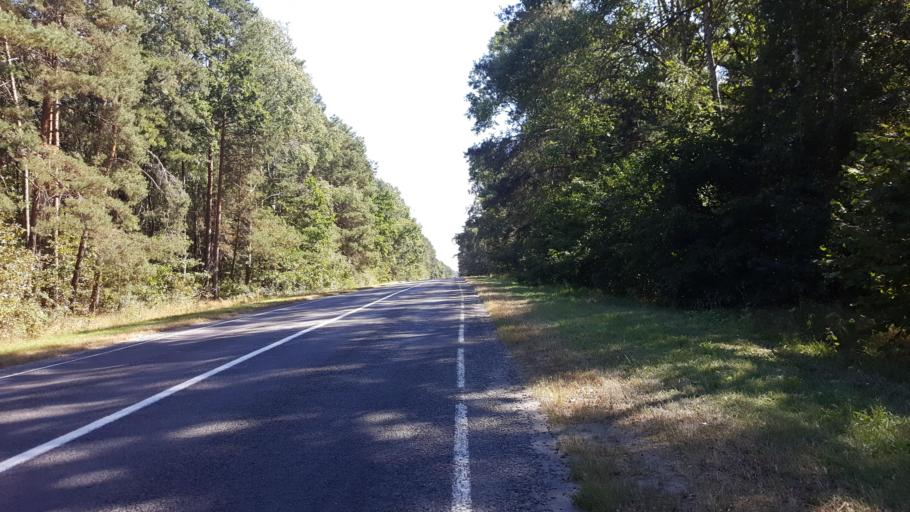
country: PL
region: Lublin Voivodeship
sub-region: Powiat bialski
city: Terespol
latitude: 52.2289
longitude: 23.5158
